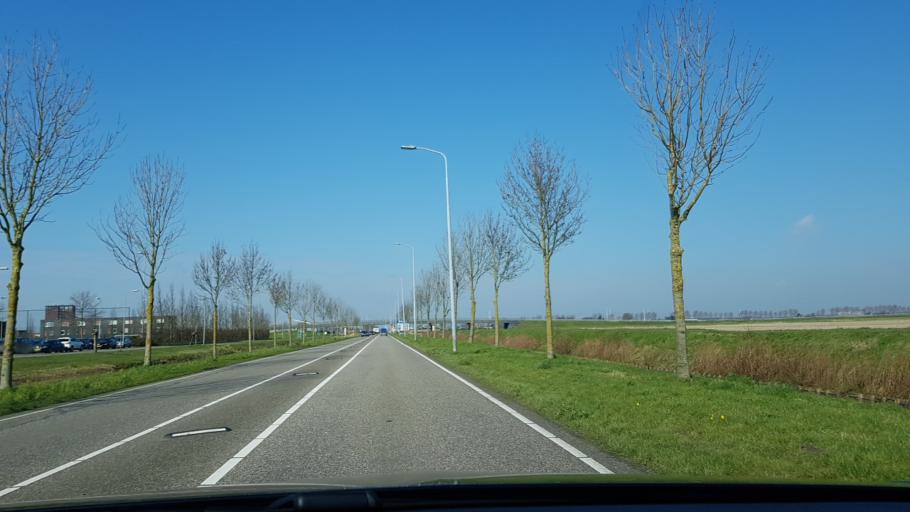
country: NL
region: South Holland
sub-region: Gemeente Hillegom
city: Hillegom
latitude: 52.2768
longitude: 4.6382
